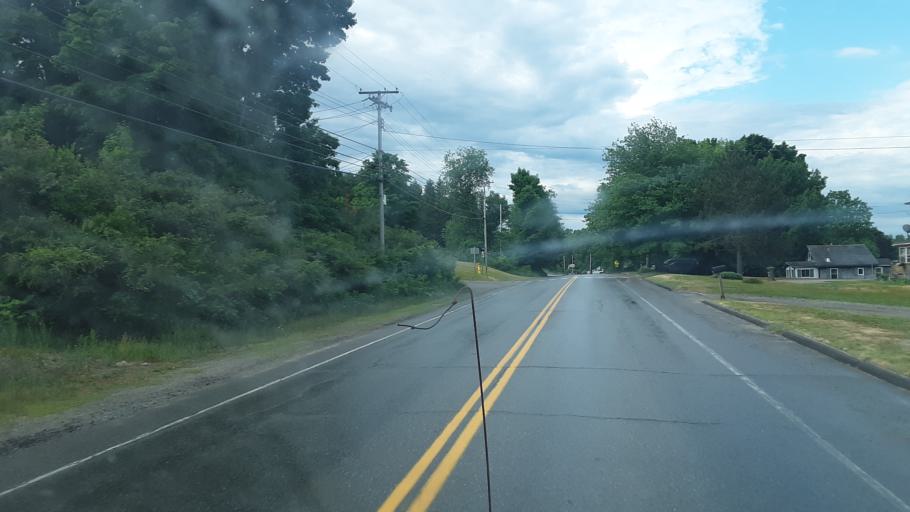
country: US
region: Maine
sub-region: Penobscot County
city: Lincoln
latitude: 45.3798
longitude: -68.4999
